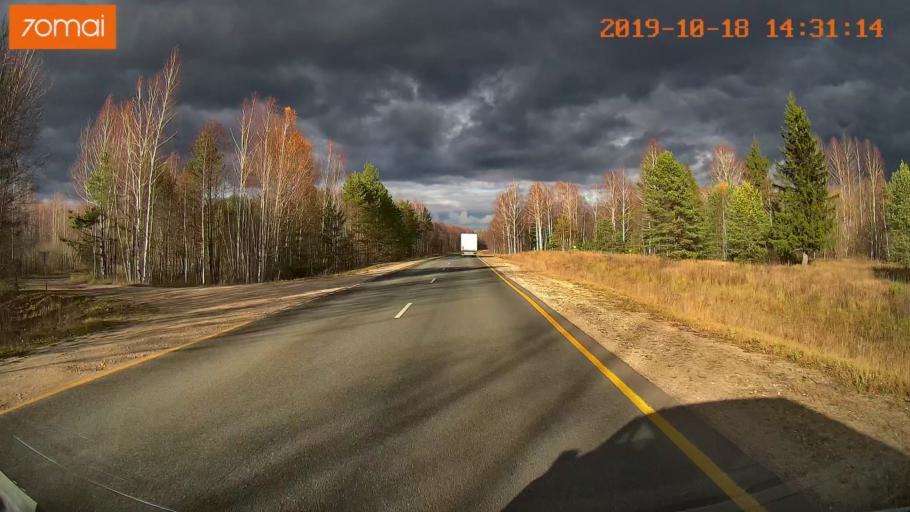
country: RU
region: Rjazan
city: Tuma
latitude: 55.1801
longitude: 40.5691
